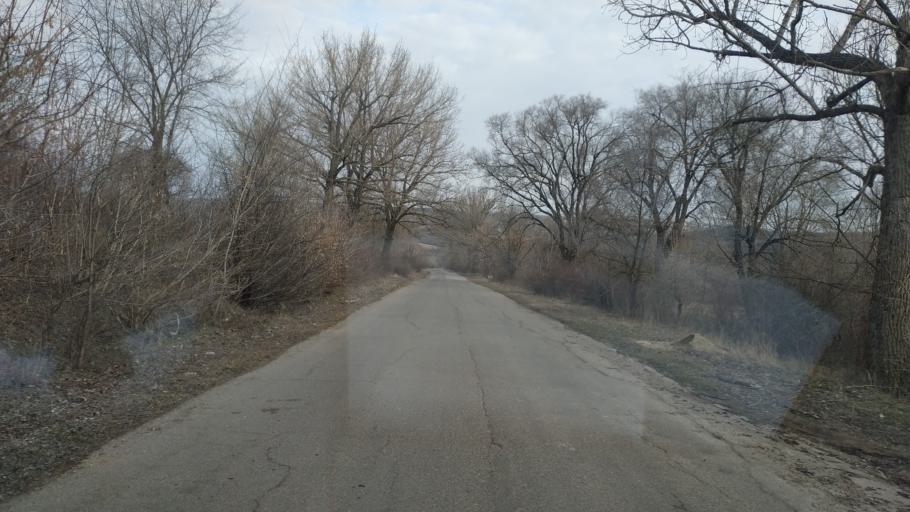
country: MD
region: Chisinau
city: Vadul lui Voda
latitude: 46.9989
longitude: 29.1112
